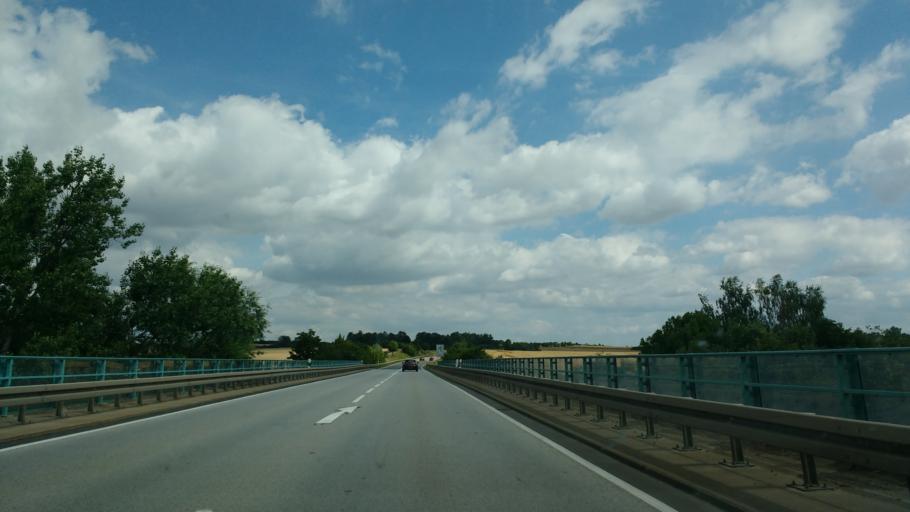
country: DE
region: Saxony-Anhalt
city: Theissen
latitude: 51.0581
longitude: 12.0995
